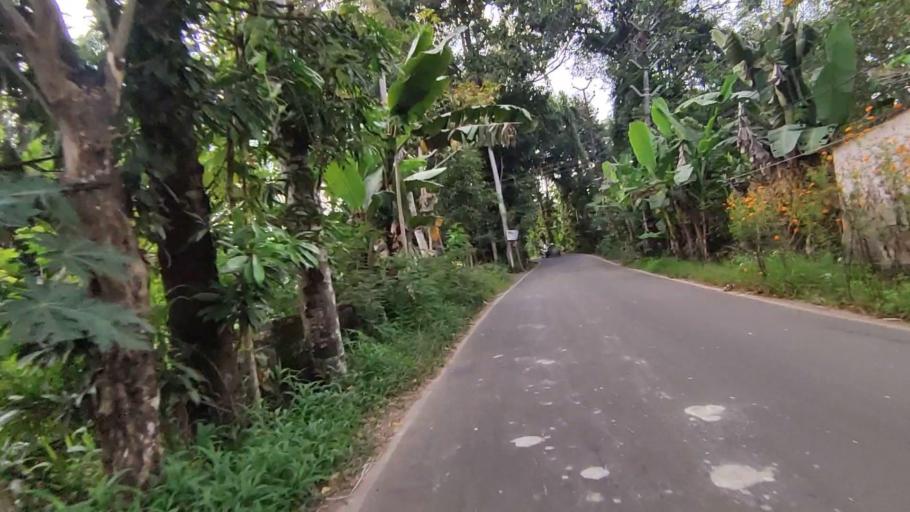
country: IN
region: Kerala
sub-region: Kottayam
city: Kottayam
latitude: 9.6007
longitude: 76.4946
